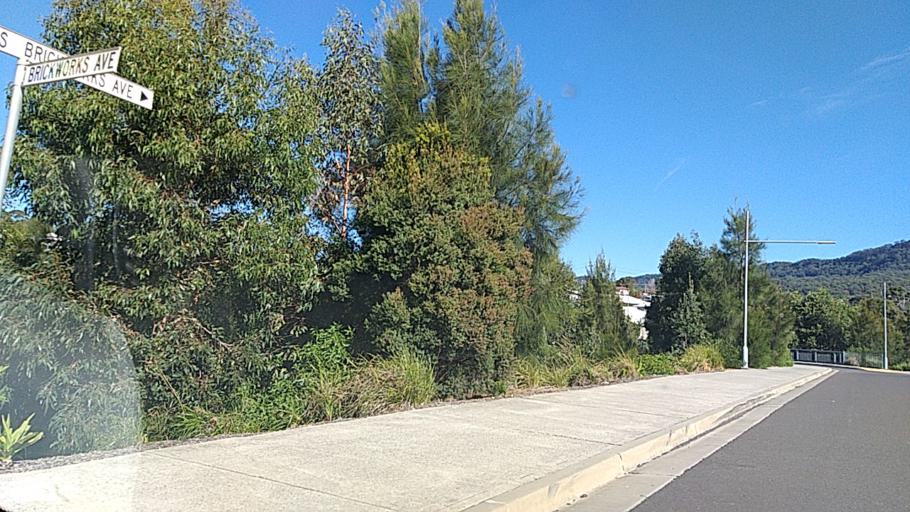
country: AU
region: New South Wales
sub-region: Wollongong
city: Bulli
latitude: -34.3229
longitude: 150.9180
